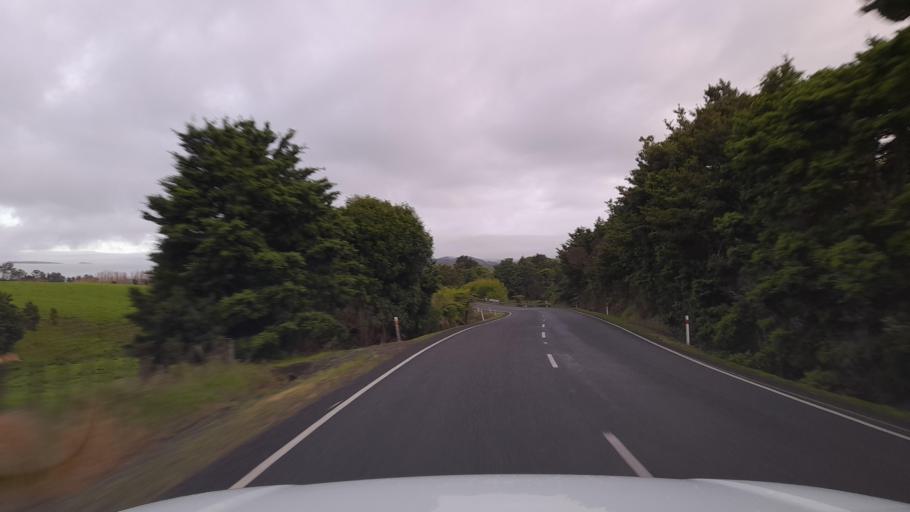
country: NZ
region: Northland
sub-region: Whangarei
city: Maungatapere
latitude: -35.7243
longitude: 174.0425
